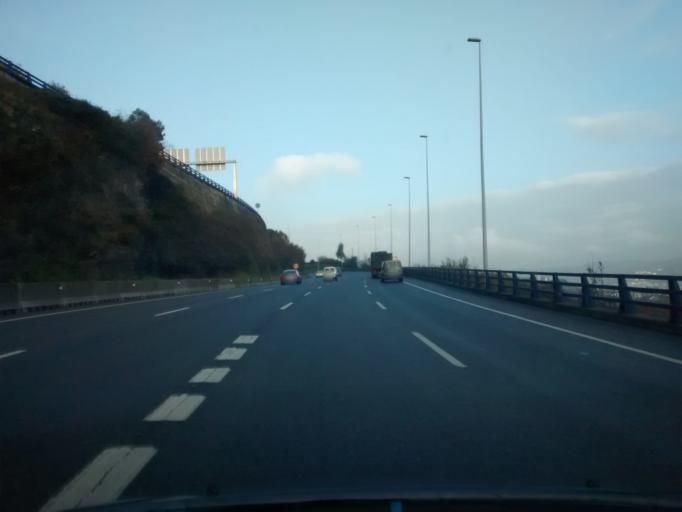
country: ES
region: Basque Country
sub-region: Bizkaia
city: Santutxu
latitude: 43.2360
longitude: -2.9191
